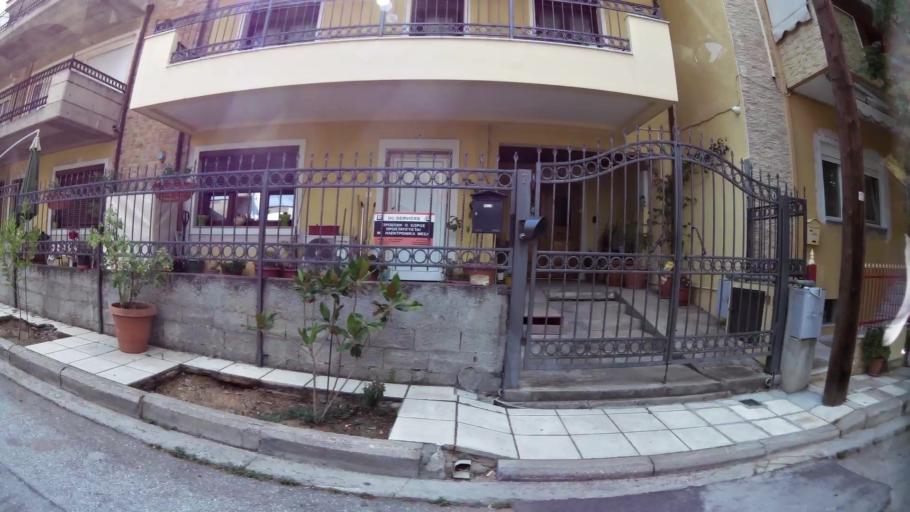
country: GR
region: Central Macedonia
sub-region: Nomos Thessalonikis
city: Polichni
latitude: 40.6686
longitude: 22.9468
